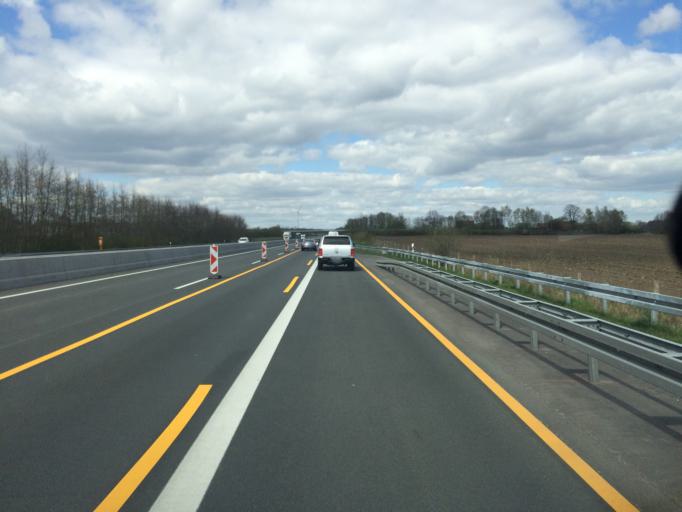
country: DE
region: North Rhine-Westphalia
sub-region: Regierungsbezirk Munster
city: Gescher
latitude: 51.9510
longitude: 7.0462
